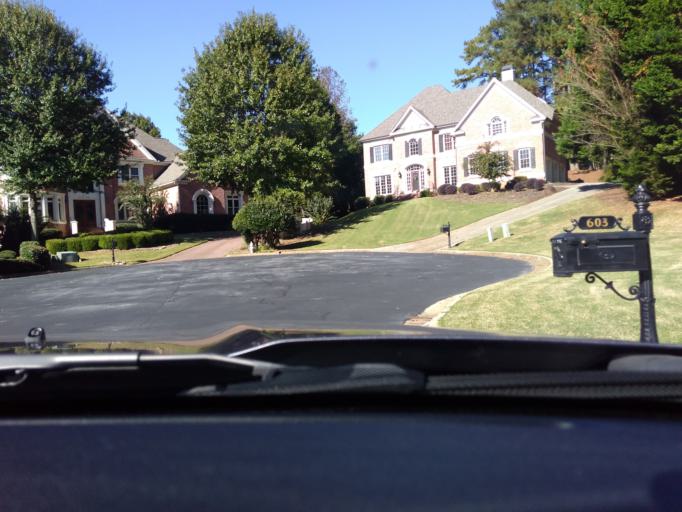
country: US
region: Georgia
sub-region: Fulton County
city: Johns Creek
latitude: 34.0190
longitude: -84.1859
